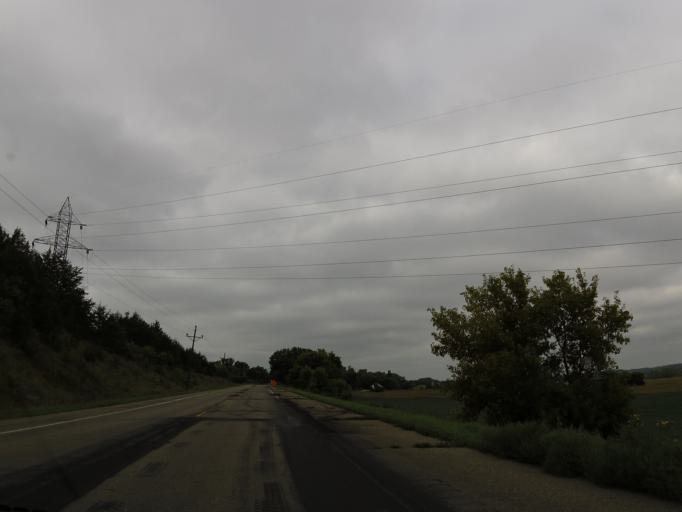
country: US
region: Minnesota
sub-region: Yellow Medicine County
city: Granite Falls
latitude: 44.8244
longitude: -95.5961
